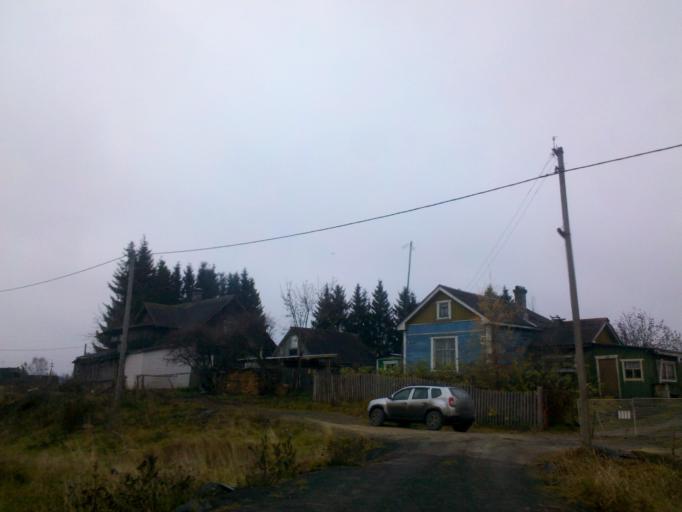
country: RU
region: Republic of Karelia
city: Shuya
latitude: 61.8195
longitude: 34.0828
